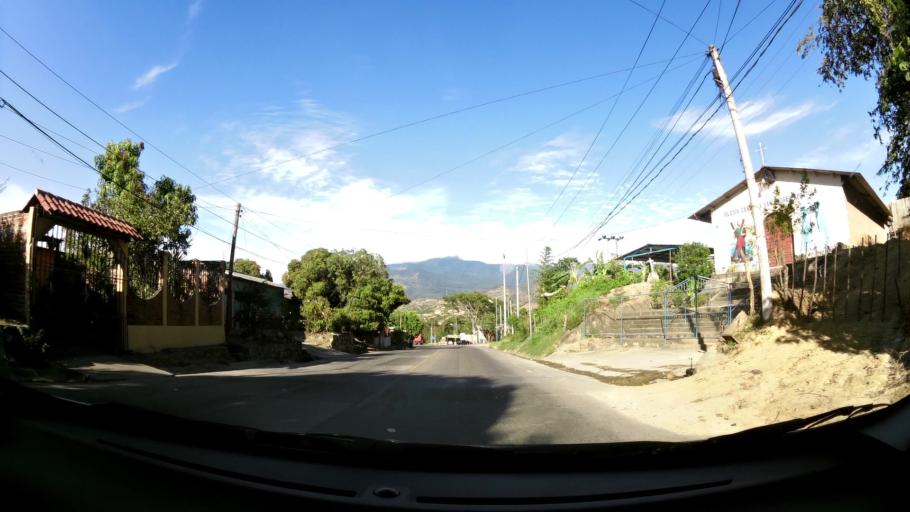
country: SV
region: Santa Ana
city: Metapan
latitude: 14.3177
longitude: -89.4460
